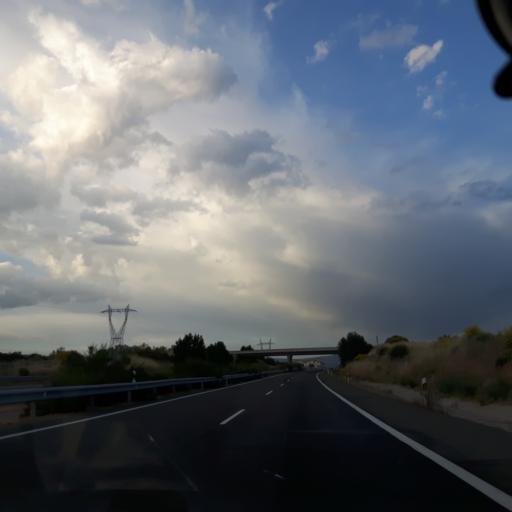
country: ES
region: Castille and Leon
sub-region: Provincia de Salamanca
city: Fuentes de Bejar
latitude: 40.5004
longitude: -5.6759
